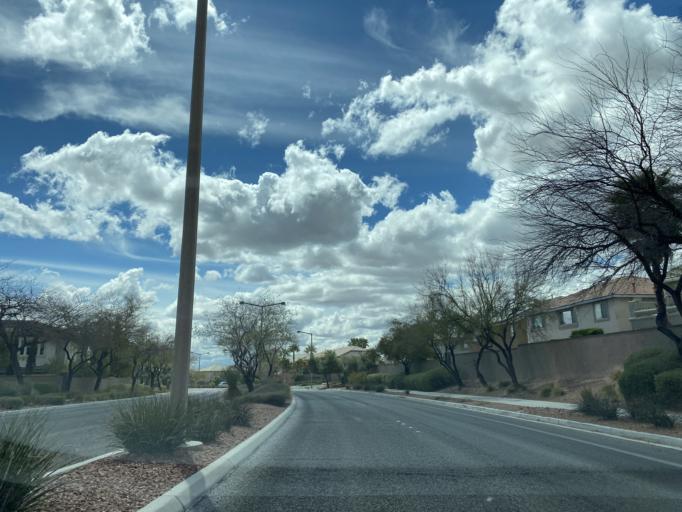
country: US
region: Nevada
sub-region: Clark County
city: Summerlin South
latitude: 36.1356
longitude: -115.3330
